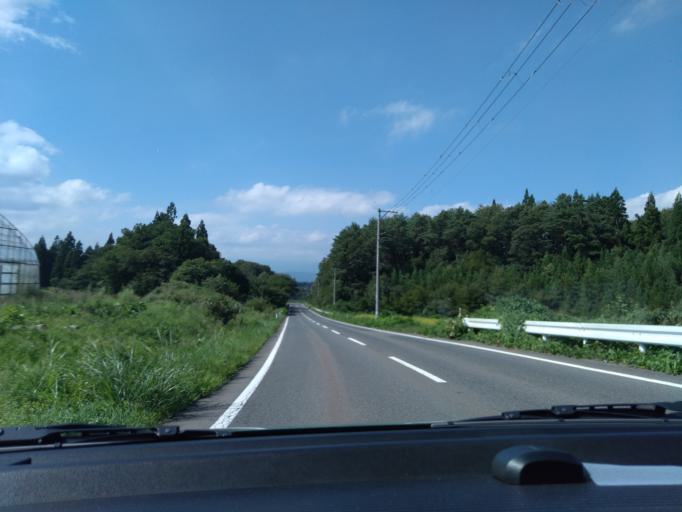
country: JP
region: Iwate
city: Shizukuishi
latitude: 39.6415
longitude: 141.0043
